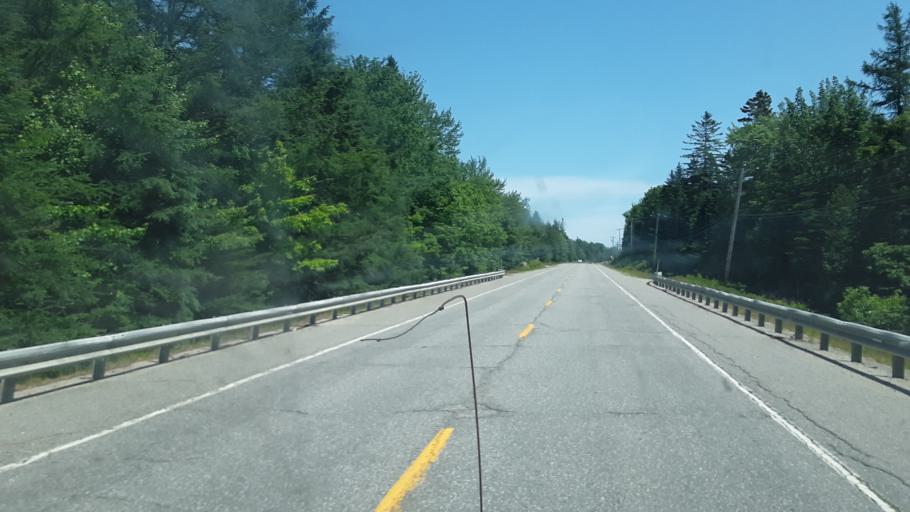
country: US
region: Maine
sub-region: Washington County
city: Steuben
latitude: 44.5114
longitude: -67.9565
